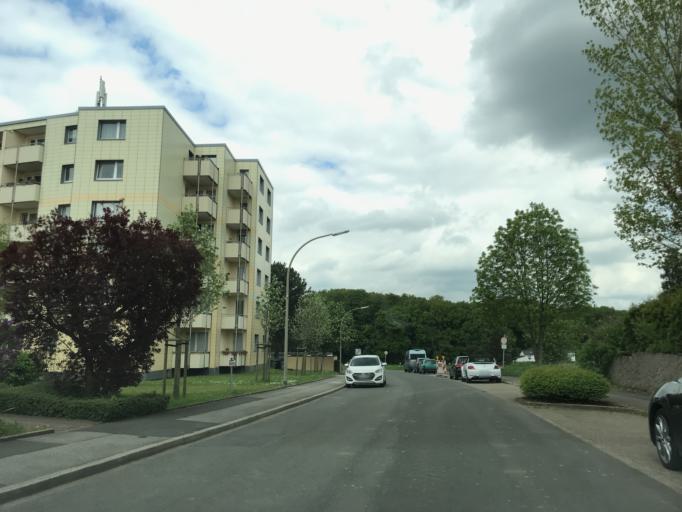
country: DE
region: North Rhine-Westphalia
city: Witten
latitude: 51.4742
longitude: 7.3733
